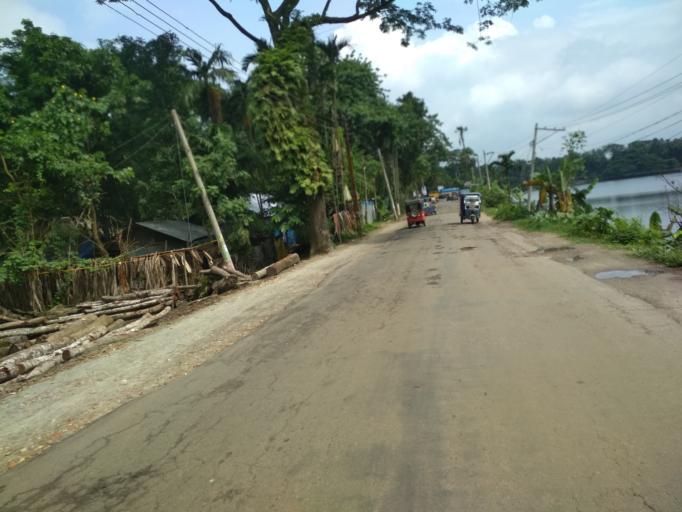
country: BD
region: Chittagong
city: Lakshmipur
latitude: 22.9657
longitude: 90.8097
